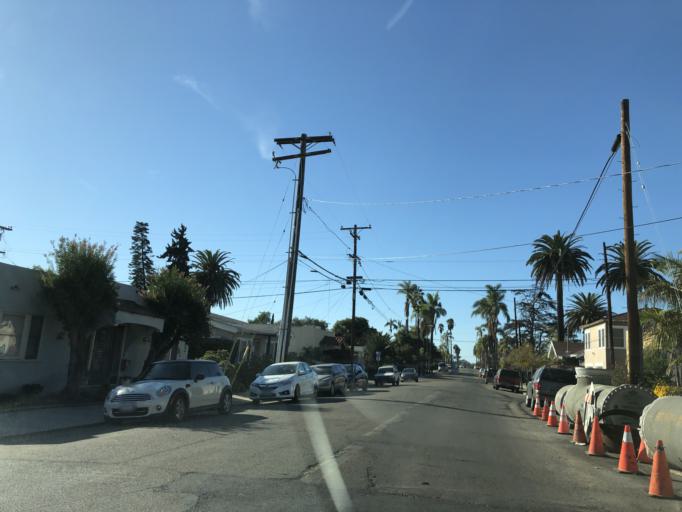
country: US
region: California
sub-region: San Diego County
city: San Diego
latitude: 32.7393
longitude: -117.1294
